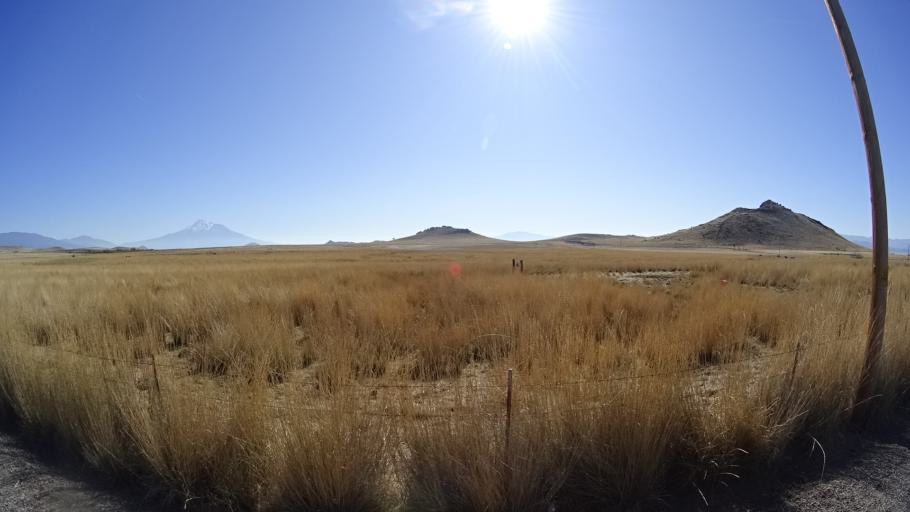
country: US
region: California
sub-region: Siskiyou County
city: Montague
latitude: 41.7566
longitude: -122.4812
